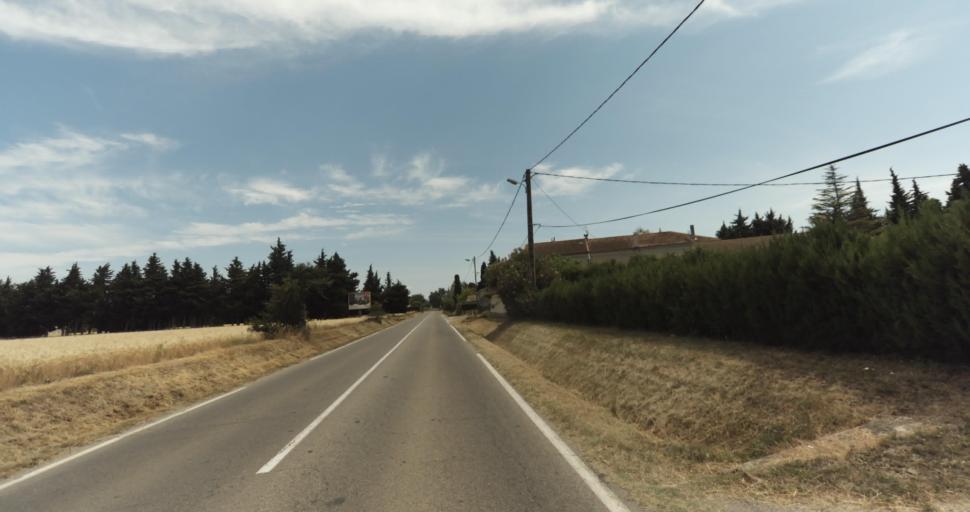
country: FR
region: Provence-Alpes-Cote d'Azur
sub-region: Departement du Vaucluse
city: Monteux
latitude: 44.0405
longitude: 4.9896
